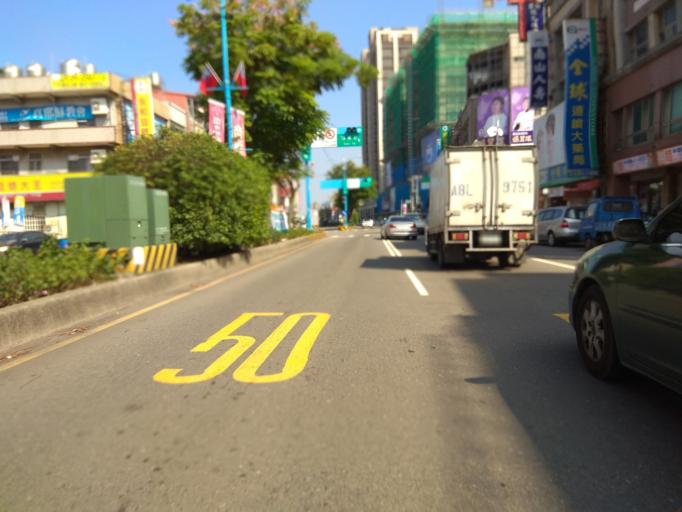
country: TW
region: Taiwan
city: Daxi
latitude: 24.9148
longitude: 121.1793
